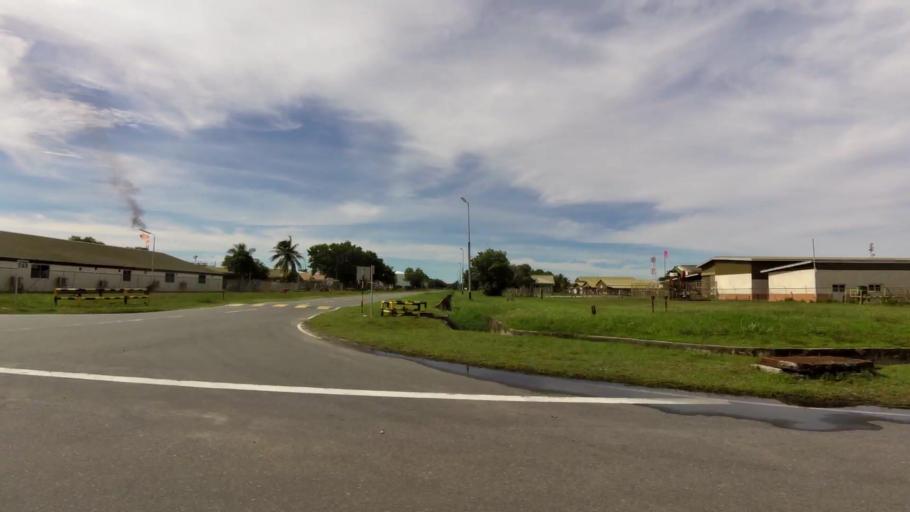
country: BN
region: Belait
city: Seria
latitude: 4.6219
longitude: 114.3361
